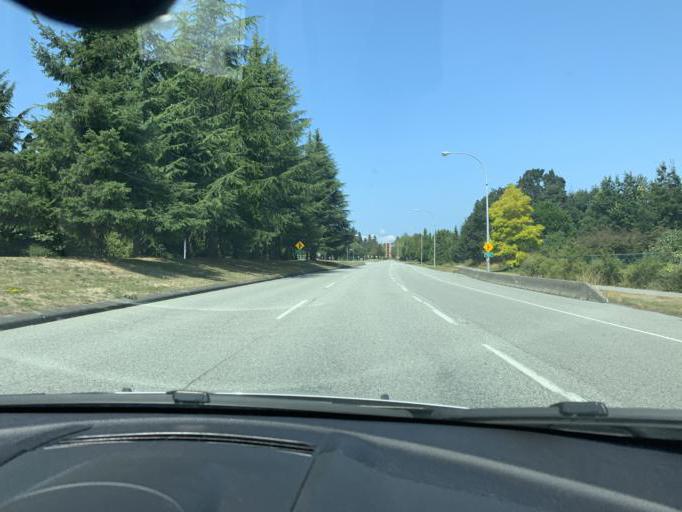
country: CA
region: British Columbia
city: West End
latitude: 49.2528
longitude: -123.2478
